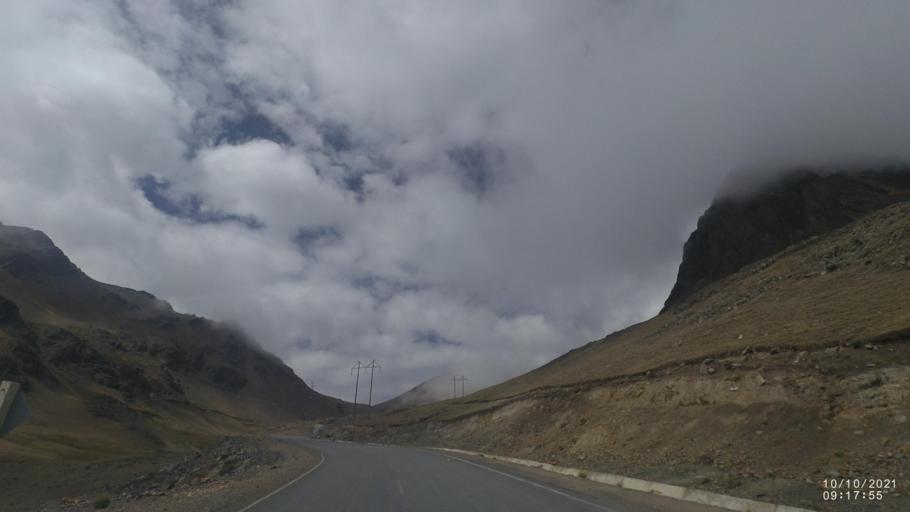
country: BO
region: La Paz
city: Quime
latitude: -17.0490
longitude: -67.2970
